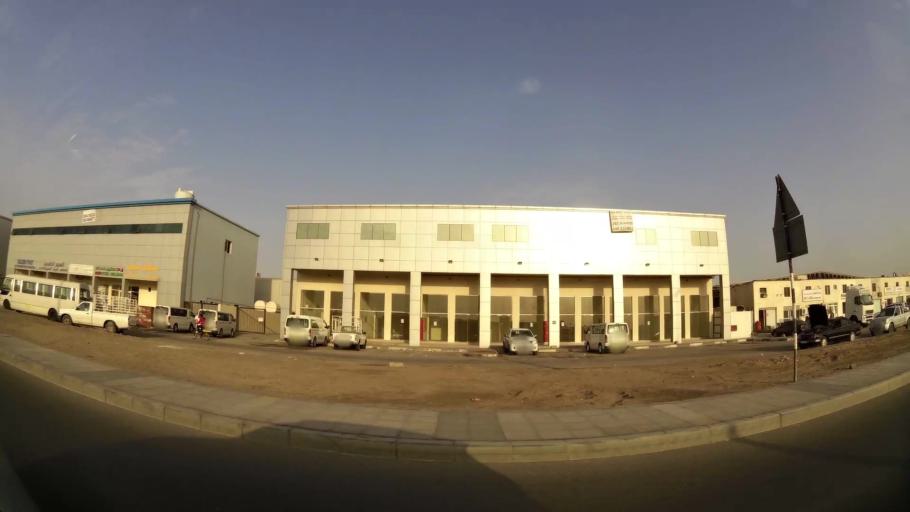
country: AE
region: Abu Dhabi
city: Abu Dhabi
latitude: 24.3656
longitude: 54.5017
